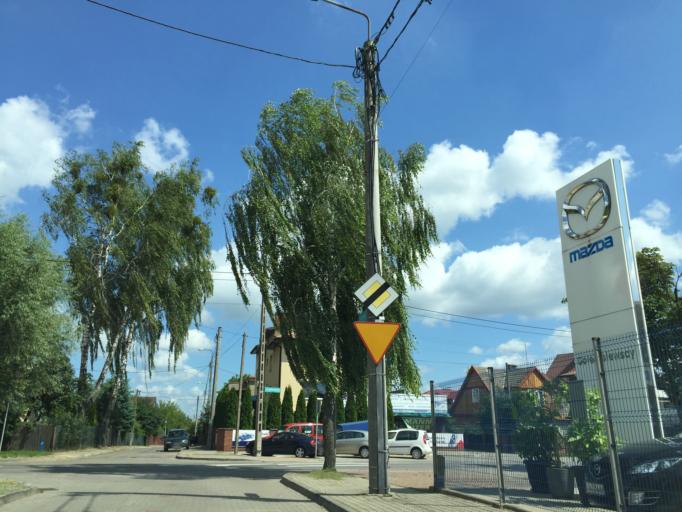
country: PL
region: Podlasie
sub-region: Bialystok
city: Bialystok
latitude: 53.1161
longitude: 23.1735
